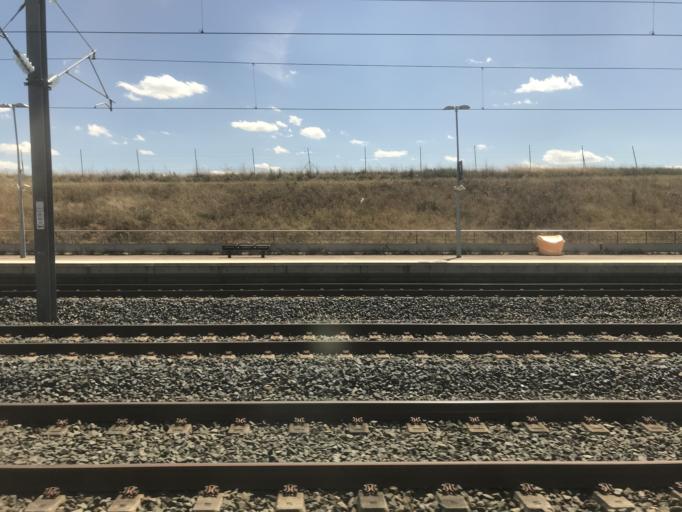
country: FR
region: Lorraine
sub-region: Departement de la Moselle
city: Verny
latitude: 48.9476
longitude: 6.1705
